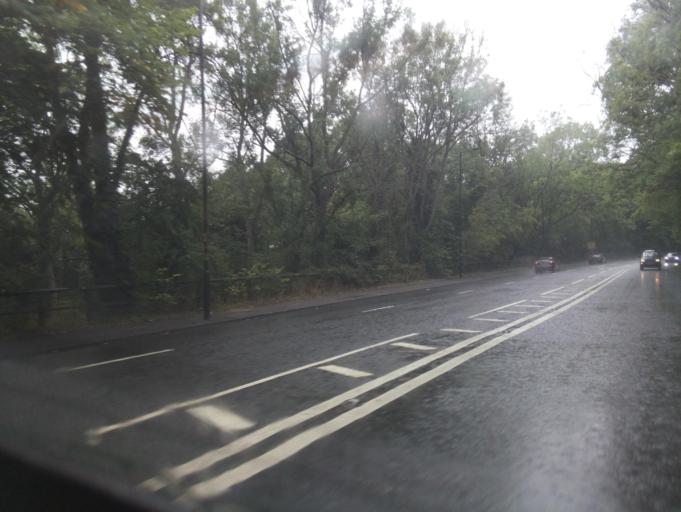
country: GB
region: England
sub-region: North Yorkshire
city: Pannal
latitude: 53.9671
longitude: -1.5281
